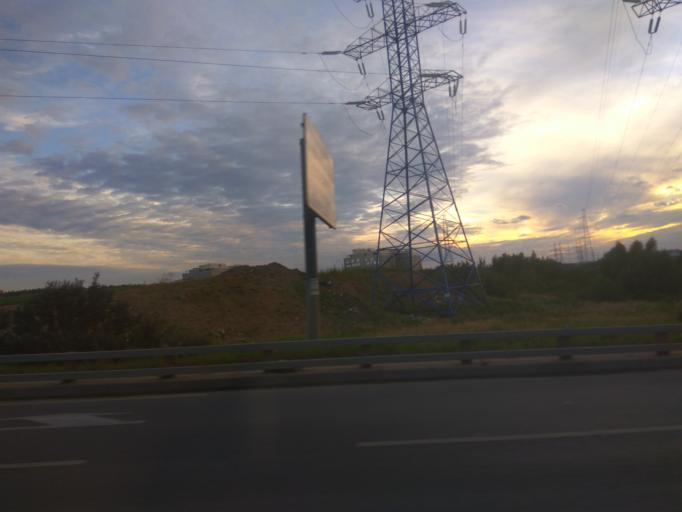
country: RU
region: Moscow
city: Solntsevo
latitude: 55.6301
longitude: 37.4214
